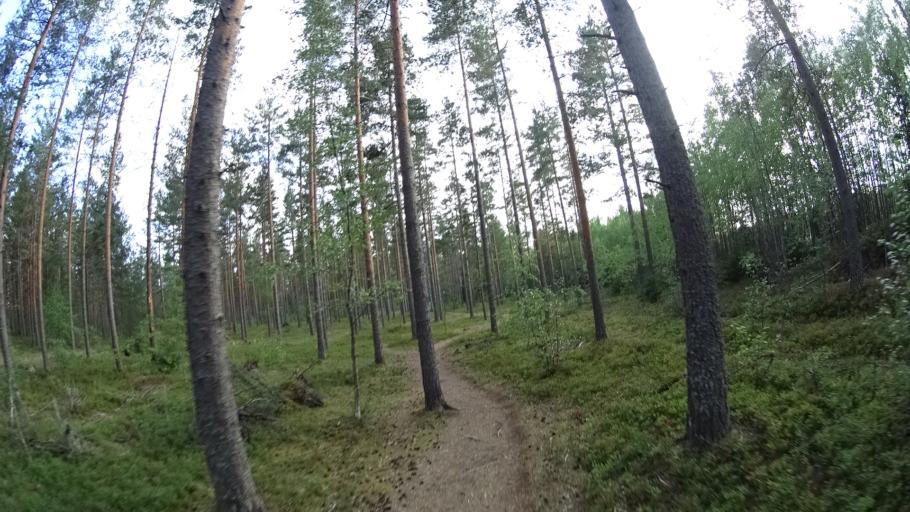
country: FI
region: Uusimaa
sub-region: Helsinki
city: Vihti
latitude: 60.3310
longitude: 24.2919
